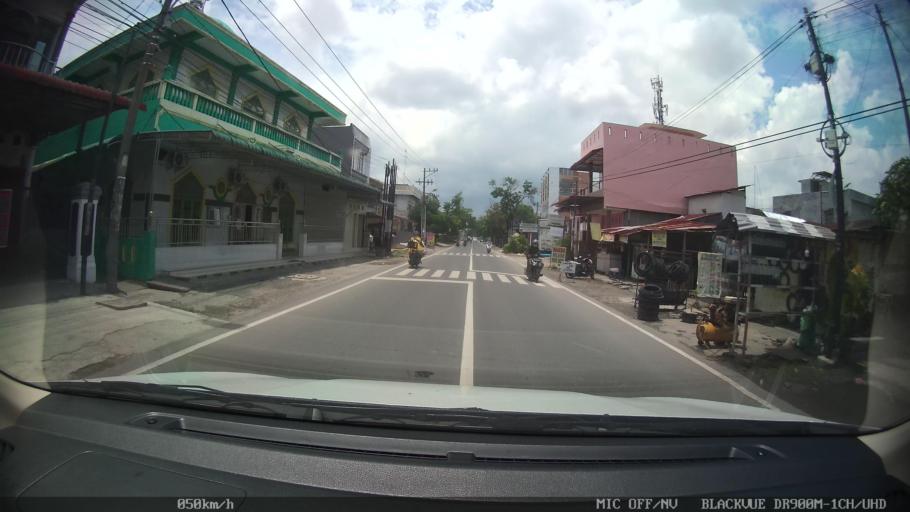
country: ID
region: North Sumatra
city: Medan
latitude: 3.6156
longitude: 98.7040
